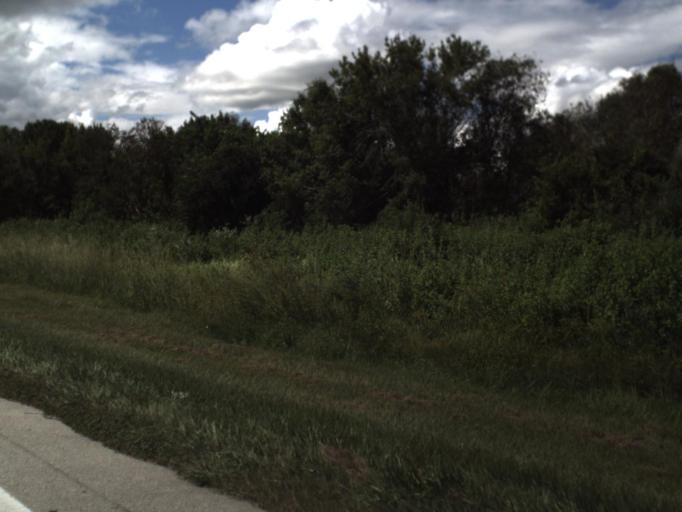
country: US
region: Florida
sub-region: Polk County
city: Mulberry
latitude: 27.7362
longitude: -81.9993
